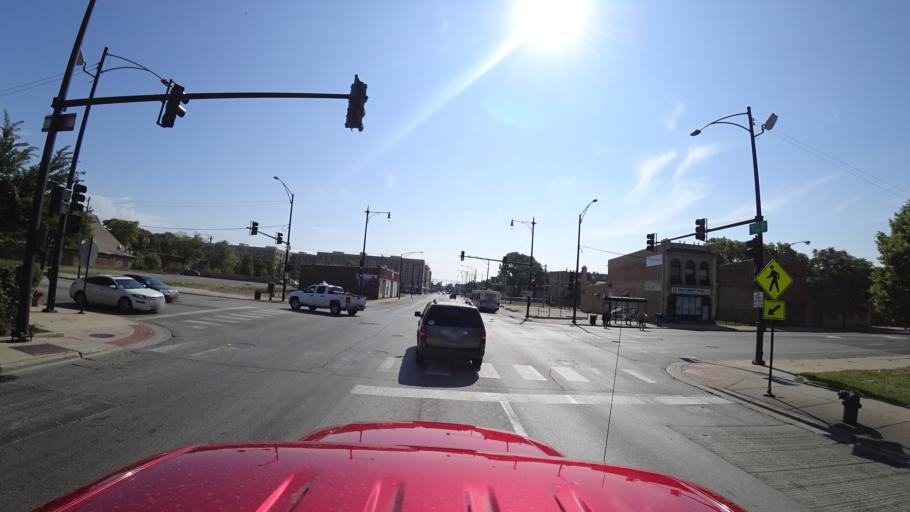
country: US
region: Illinois
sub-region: Cook County
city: Chicago
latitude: 41.8092
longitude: -87.6264
